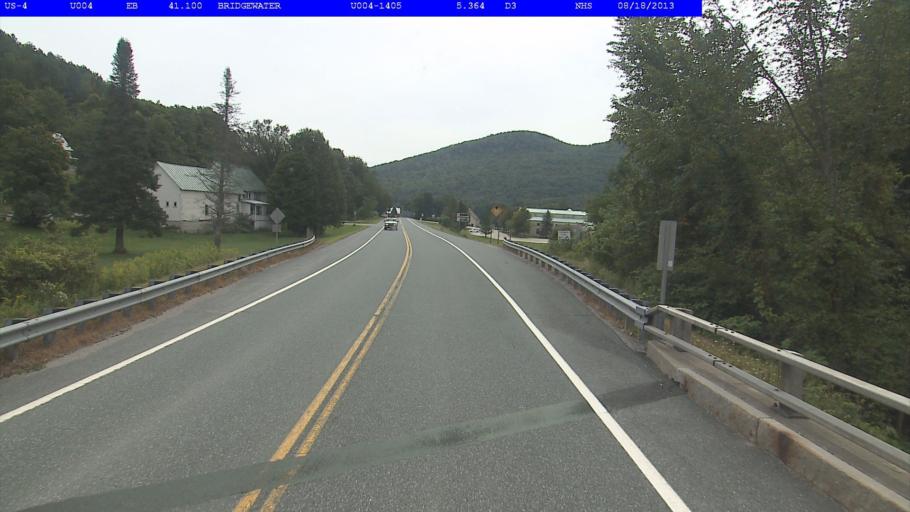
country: US
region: Vermont
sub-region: Windsor County
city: Woodstock
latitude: 43.5898
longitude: -72.6616
